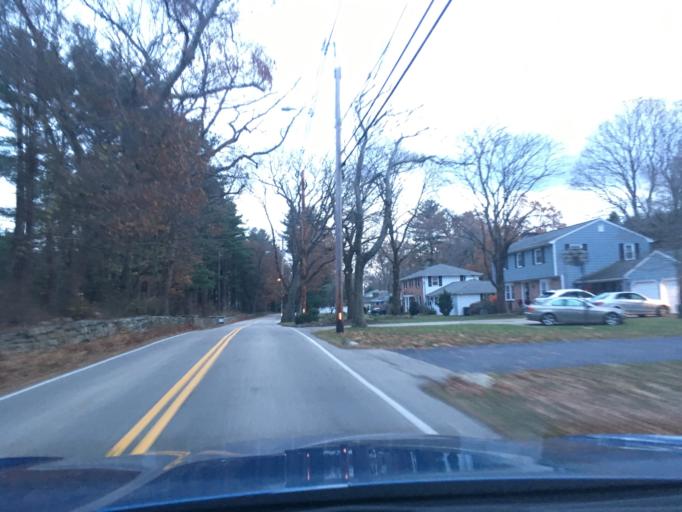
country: US
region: Rhode Island
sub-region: Kent County
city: East Greenwich
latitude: 41.6794
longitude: -71.4598
